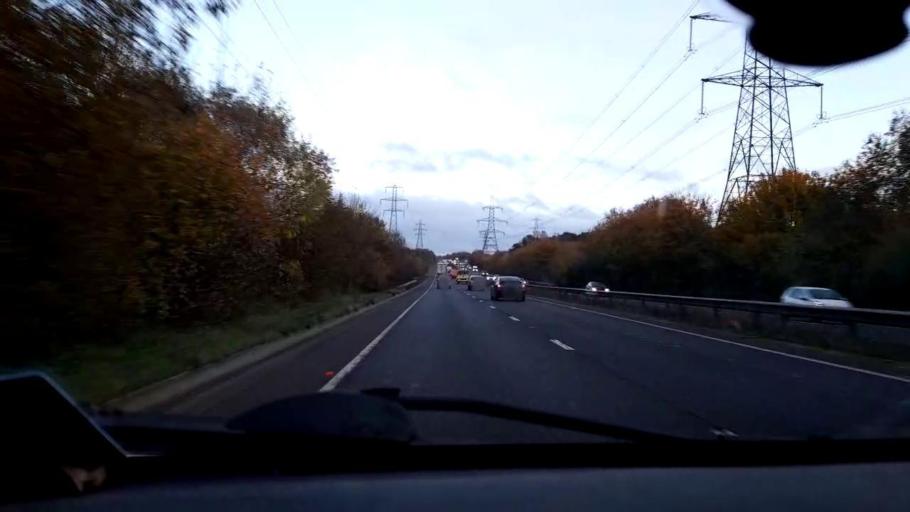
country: GB
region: England
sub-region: Norfolk
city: Cringleford
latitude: 52.5929
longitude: 1.2441
